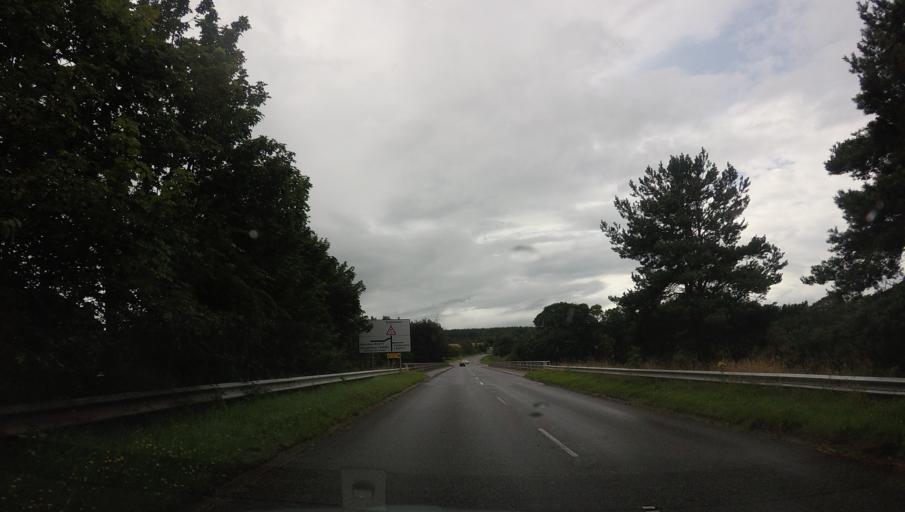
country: GB
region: Scotland
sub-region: Aberdeenshire
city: Banchory
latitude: 57.0536
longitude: -2.4097
